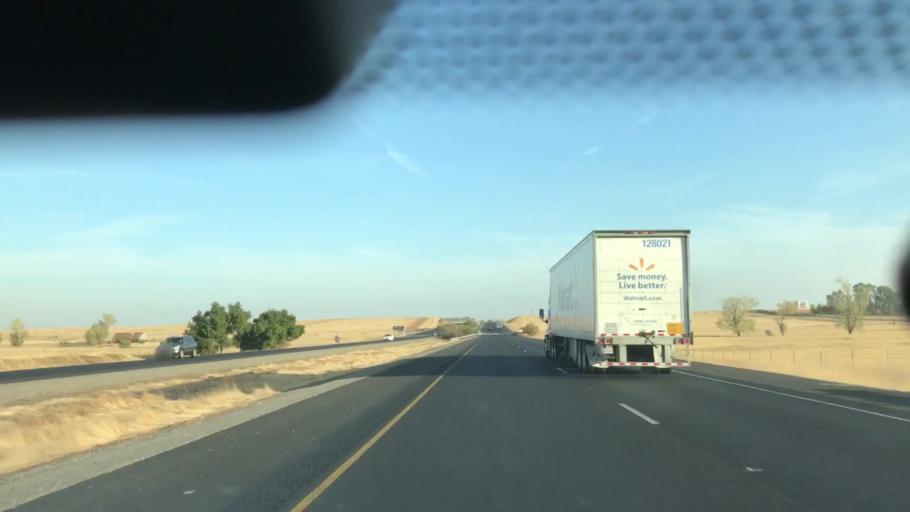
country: US
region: California
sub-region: Glenn County
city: Orland
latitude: 39.8126
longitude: -122.1998
